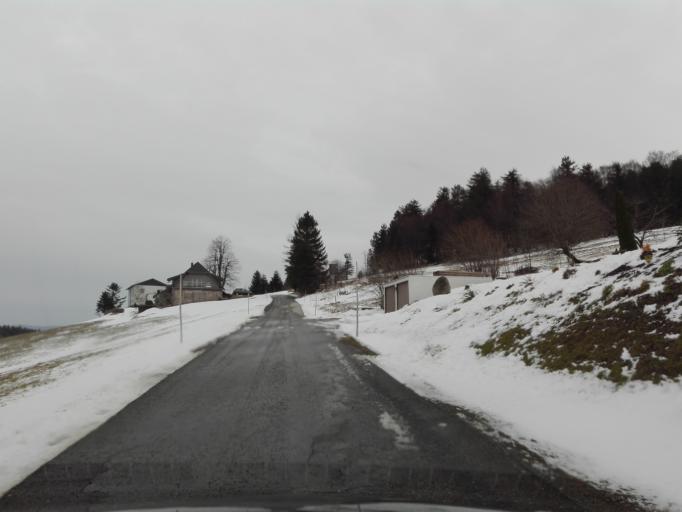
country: AT
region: Upper Austria
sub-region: Politischer Bezirk Rohrbach
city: Pfarrkirchen im Muehlkreis
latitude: 48.5600
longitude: 13.8290
